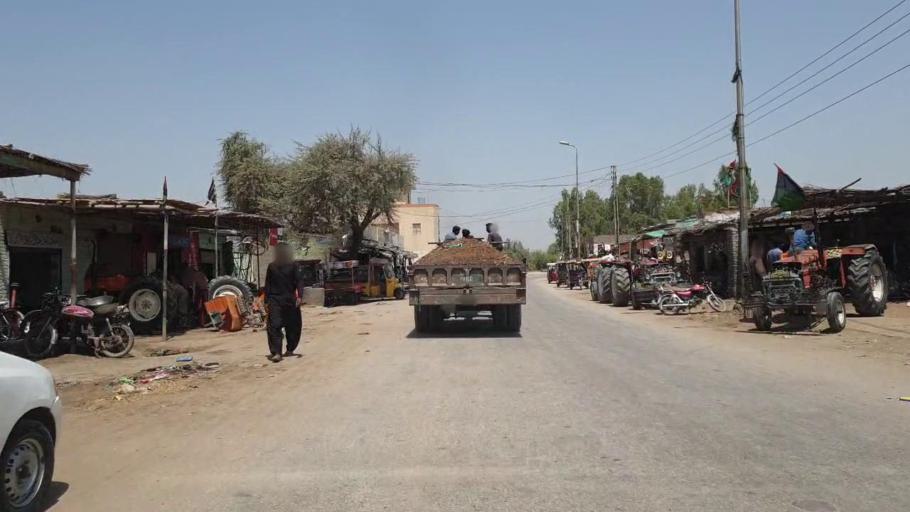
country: PK
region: Sindh
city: Adilpur
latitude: 27.9389
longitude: 69.3192
